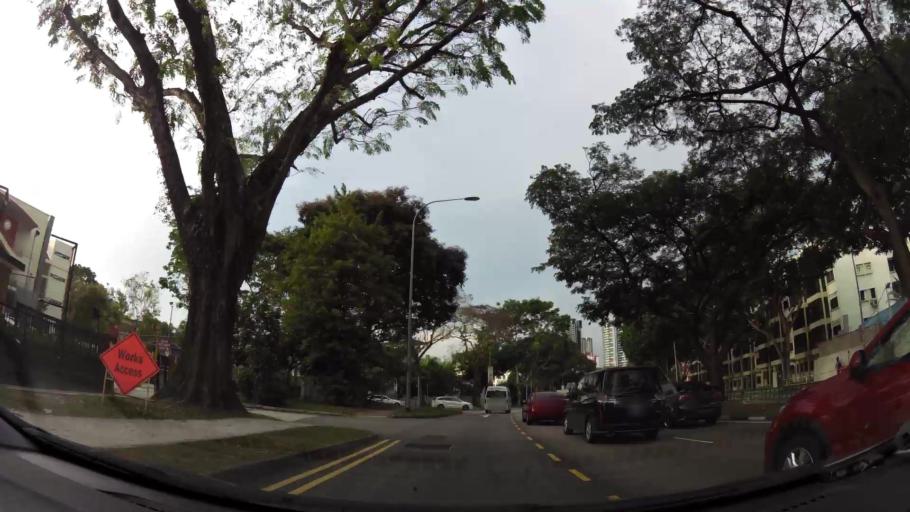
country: SG
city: Singapore
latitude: 1.3219
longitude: 103.8416
